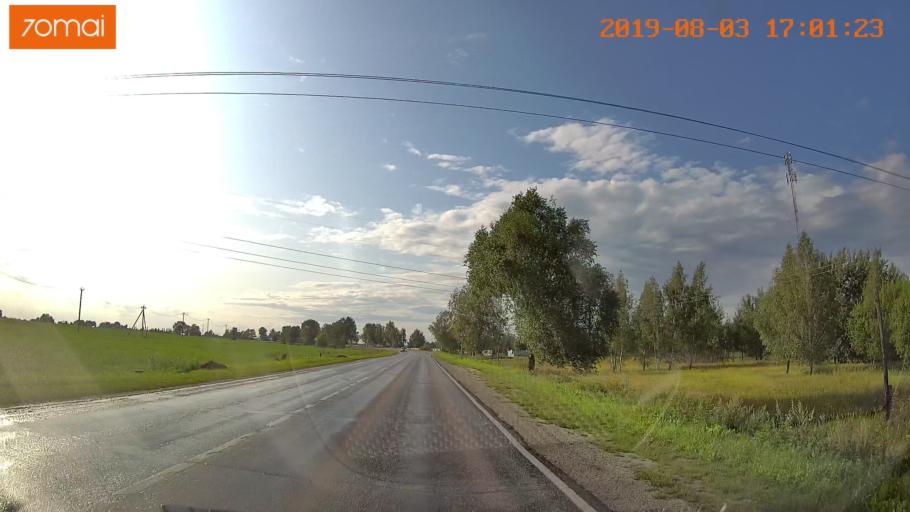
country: RU
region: Moskovskaya
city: Voskresensk
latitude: 55.3447
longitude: 38.6040
